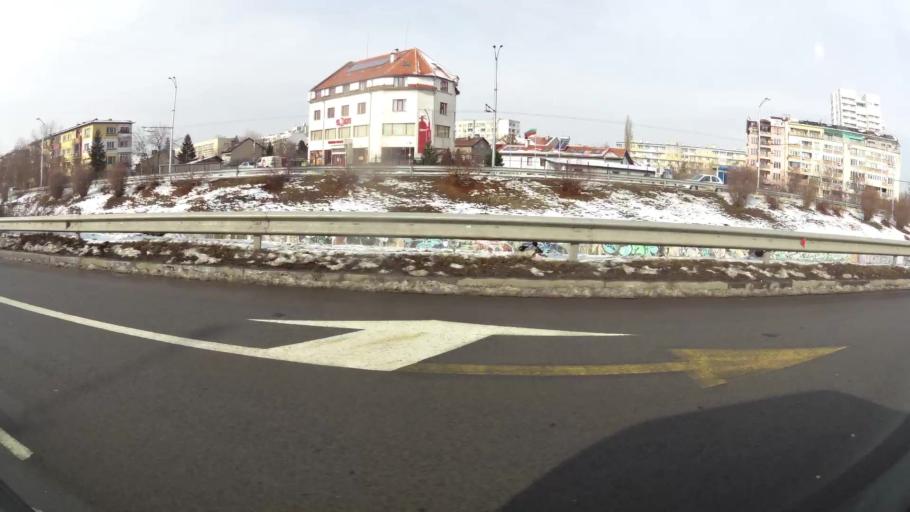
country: BG
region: Sofia-Capital
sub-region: Stolichna Obshtina
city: Sofia
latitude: 42.7064
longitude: 23.3622
